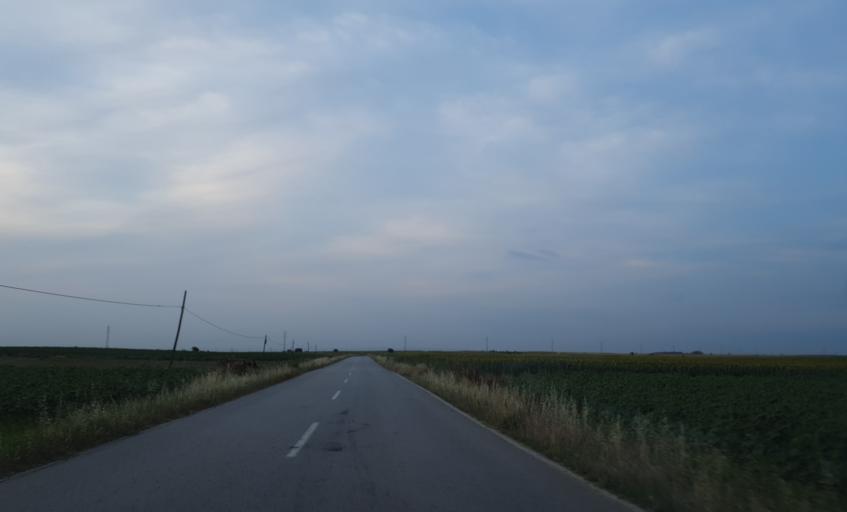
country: TR
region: Kirklareli
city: Buyukkaristiran
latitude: 41.3250
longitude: 27.6064
